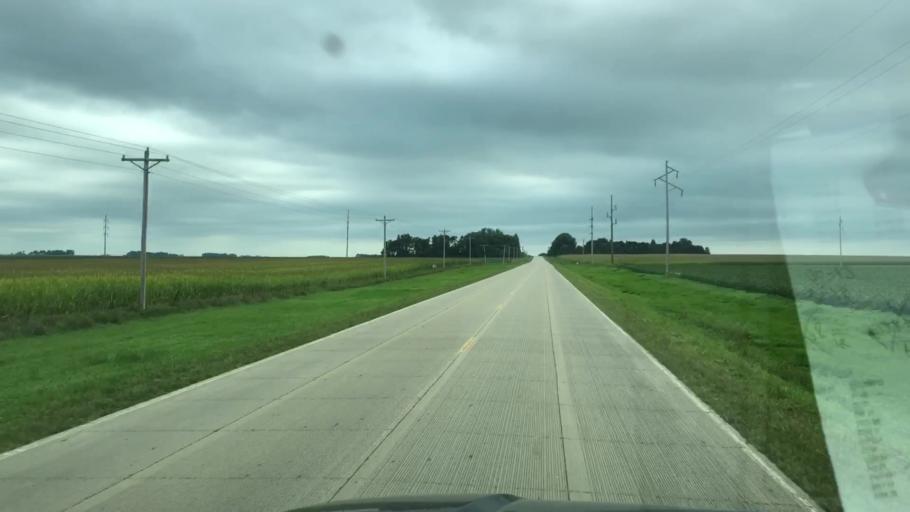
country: US
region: Iowa
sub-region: O'Brien County
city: Sheldon
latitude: 43.1746
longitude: -95.9801
